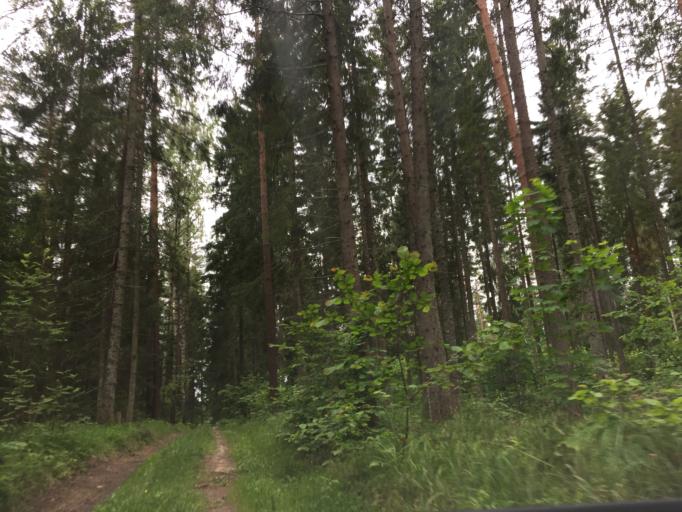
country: LV
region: Tukuma Rajons
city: Tukums
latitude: 57.0175
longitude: 23.0799
